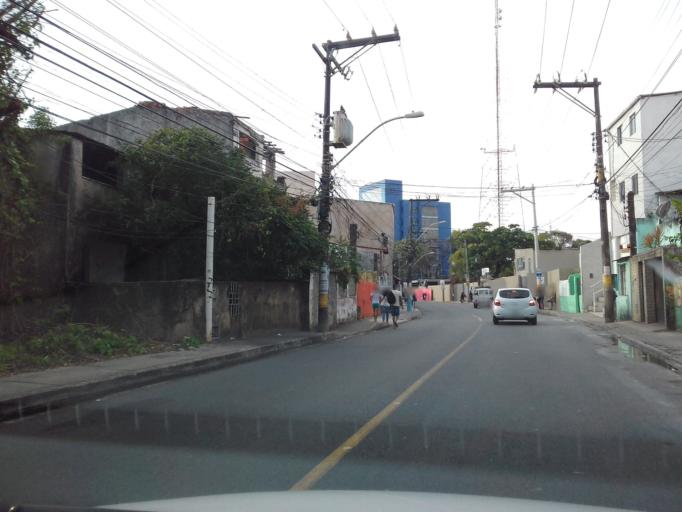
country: BR
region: Bahia
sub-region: Salvador
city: Salvador
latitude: -13.0065
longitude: -38.4971
